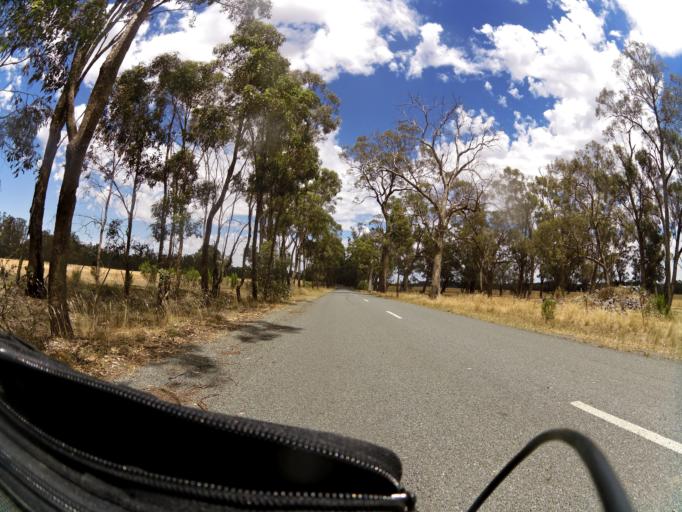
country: AU
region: Victoria
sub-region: Greater Shepparton
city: Shepparton
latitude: -36.6508
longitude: 145.2062
